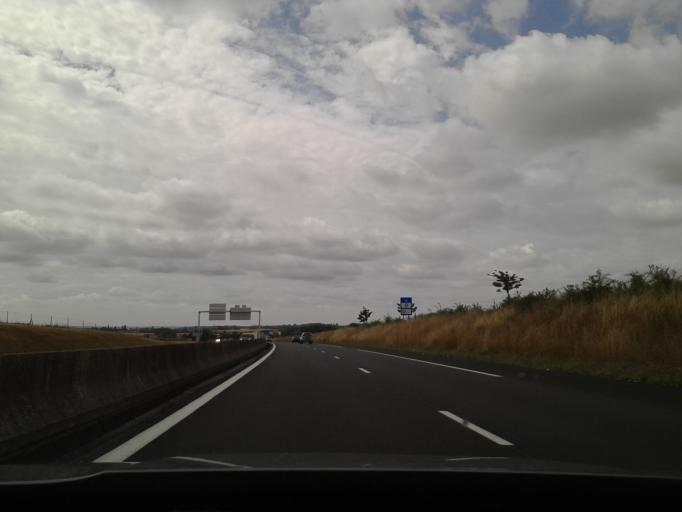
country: FR
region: Lower Normandy
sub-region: Departement de l'Orne
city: Sees
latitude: 48.6201
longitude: 0.1914
